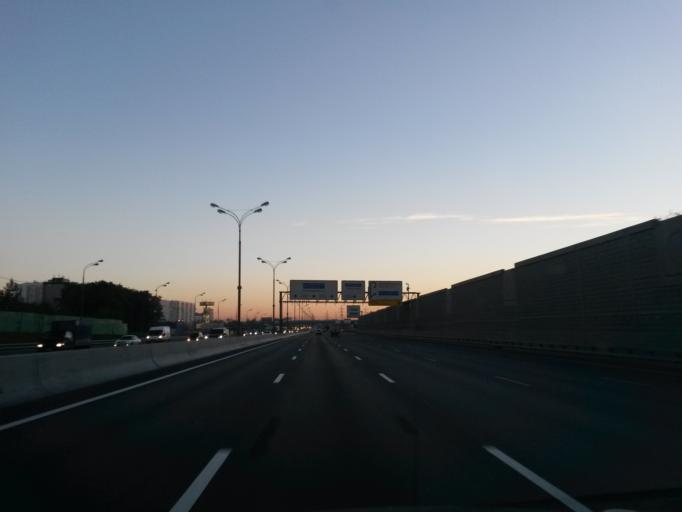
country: RU
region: Moscow
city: Vostochnyy
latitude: 55.8078
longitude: 37.8396
